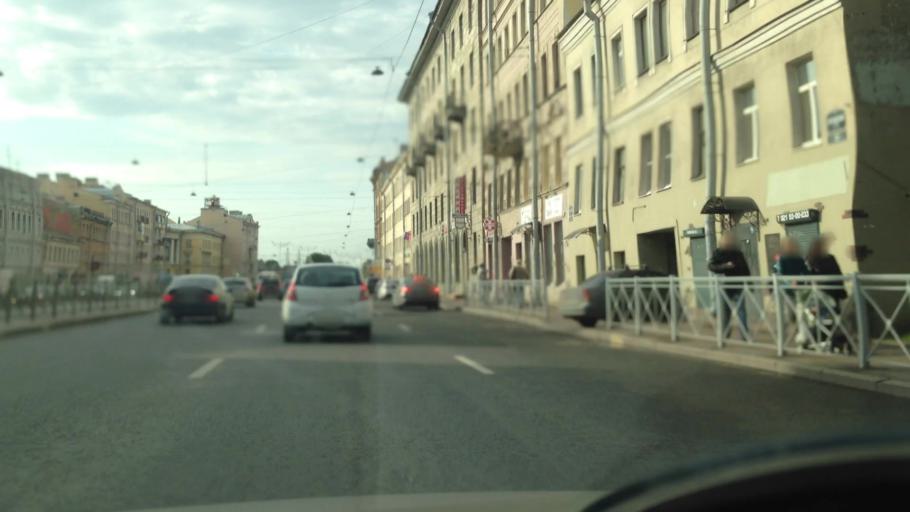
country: RU
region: St.-Petersburg
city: Centralniy
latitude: 59.9095
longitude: 30.3466
